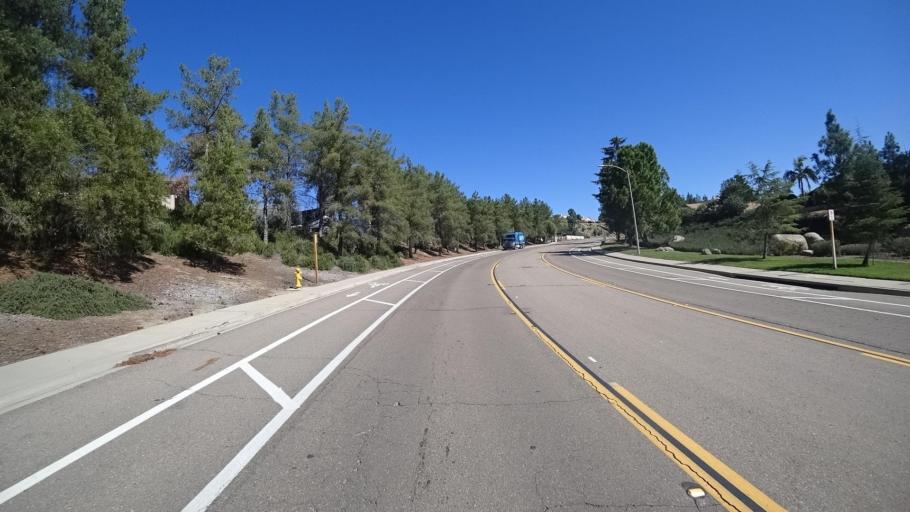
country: US
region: California
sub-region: San Diego County
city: Alpine
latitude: 32.8436
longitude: -116.7807
